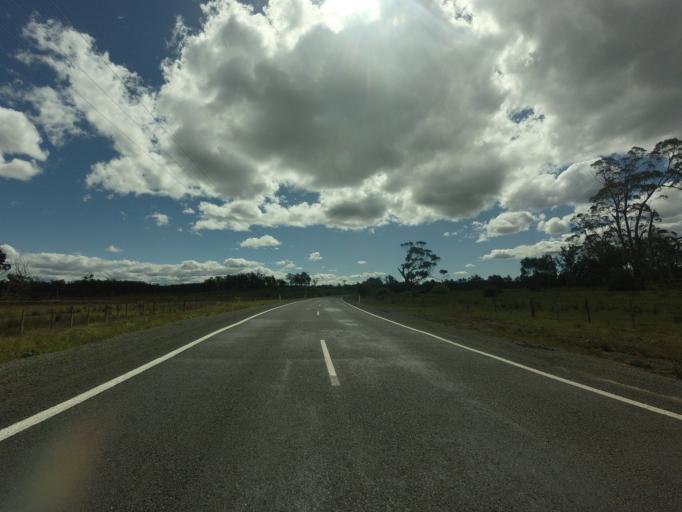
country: AU
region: Tasmania
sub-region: Northern Midlands
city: Evandale
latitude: -41.9911
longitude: 147.6803
